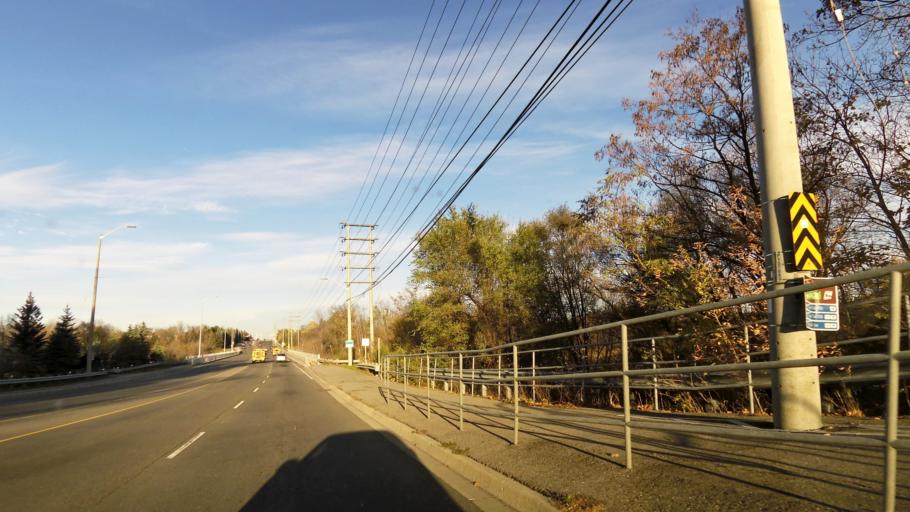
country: CA
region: Ontario
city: Mississauga
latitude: 43.5915
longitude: -79.7187
